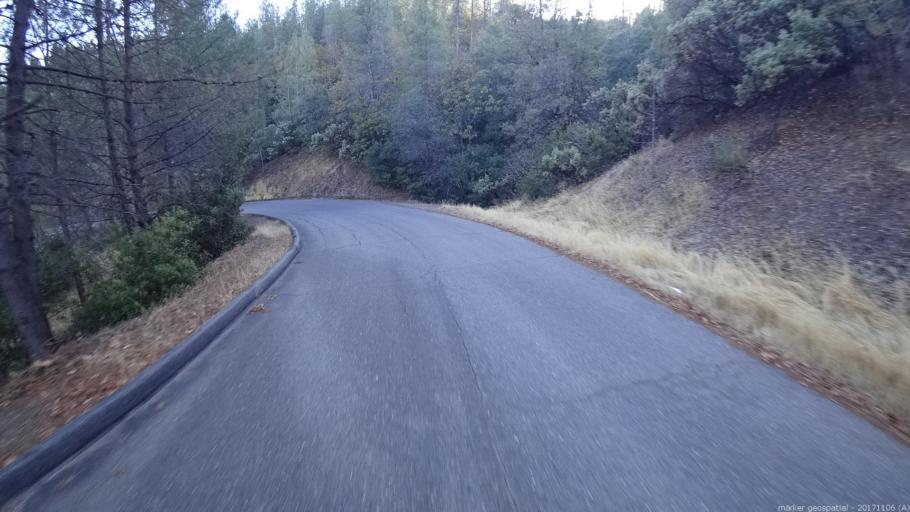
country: US
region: California
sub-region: Shasta County
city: Shasta
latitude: 40.5821
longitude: -122.4936
